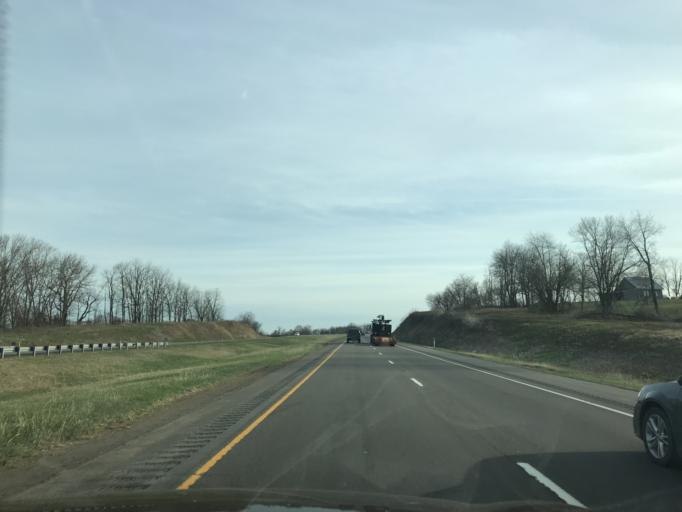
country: US
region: Pennsylvania
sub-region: Northumberland County
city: Watsontown
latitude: 41.0986
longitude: -76.8104
